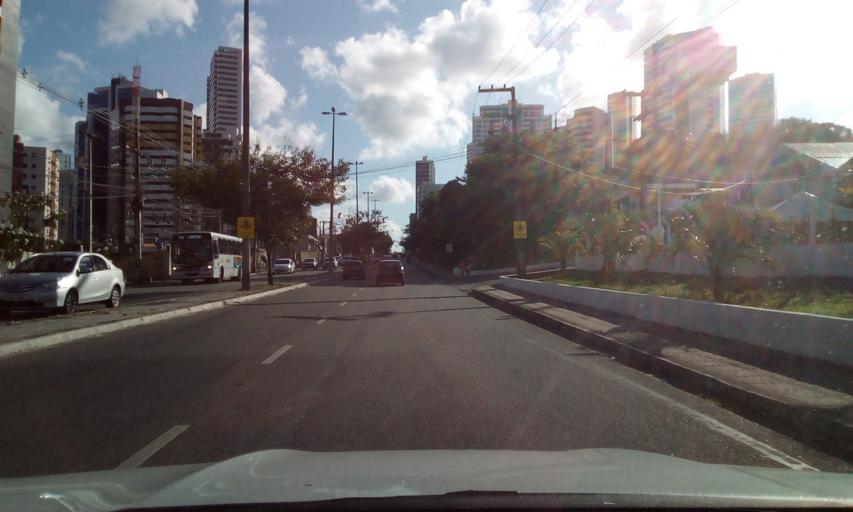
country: BR
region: Paraiba
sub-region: Joao Pessoa
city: Joao Pessoa
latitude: -7.1145
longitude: -34.8329
